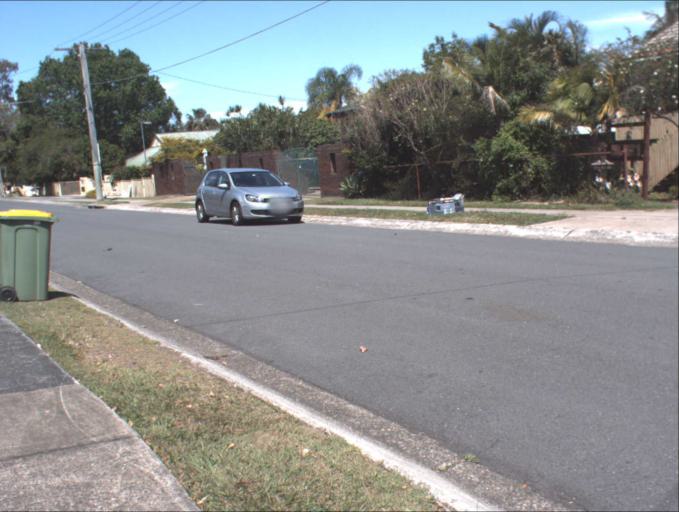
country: AU
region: Queensland
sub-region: Logan
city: Logan City
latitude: -27.6500
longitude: 153.1265
